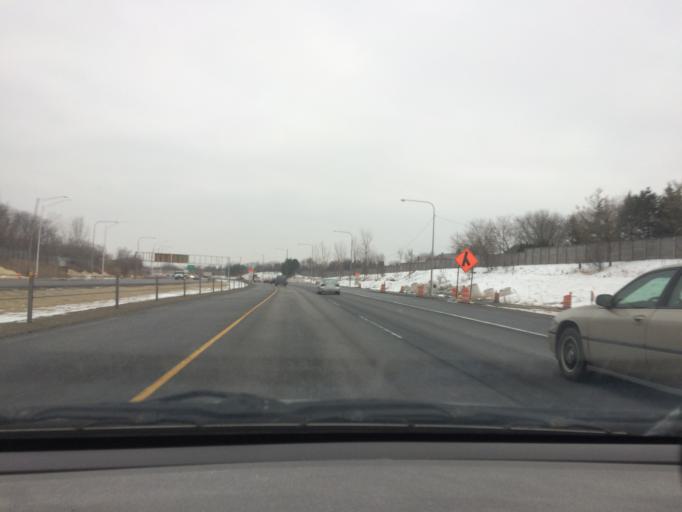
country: US
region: Illinois
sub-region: DuPage County
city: Roselle
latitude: 41.9932
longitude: -88.0776
